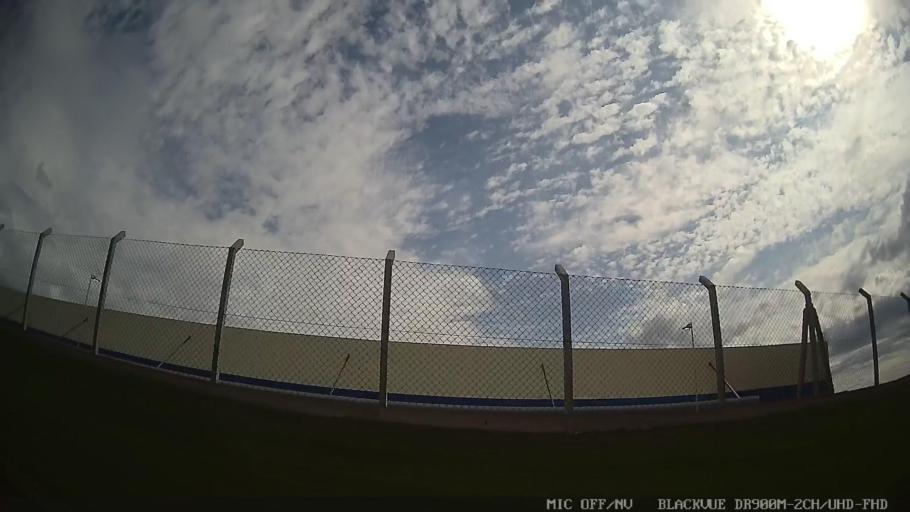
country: BR
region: Sao Paulo
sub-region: Salto
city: Salto
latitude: -23.1604
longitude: -47.2650
